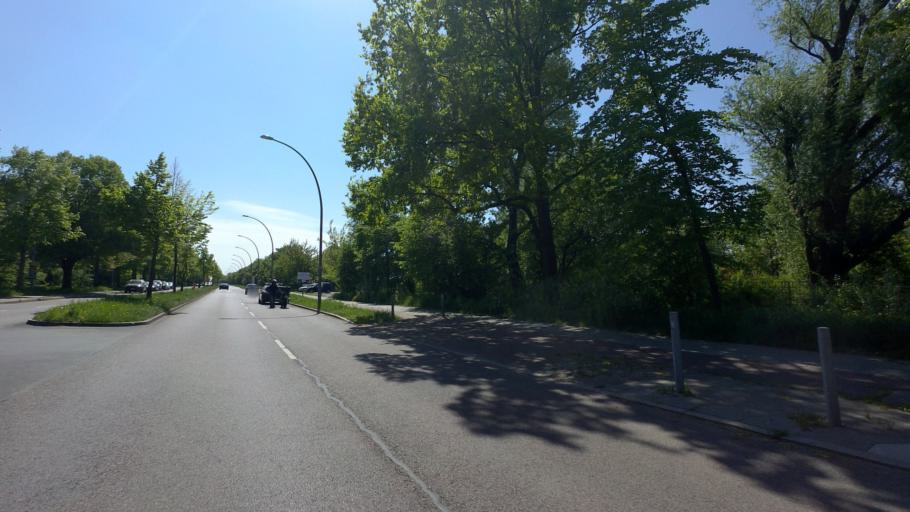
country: DE
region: Brandenburg
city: Schonefeld
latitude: 52.4076
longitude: 13.5076
